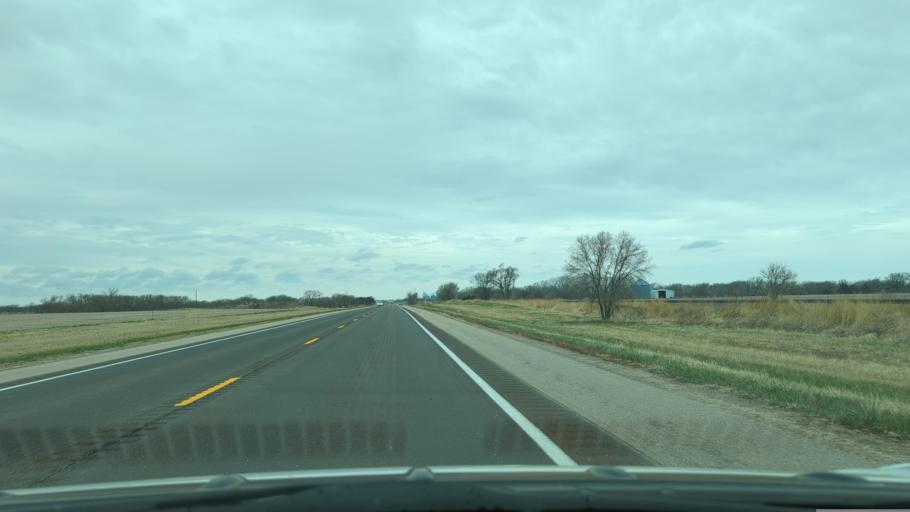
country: US
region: Nebraska
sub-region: Lancaster County
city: Waverly
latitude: 40.9416
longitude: -96.4765
